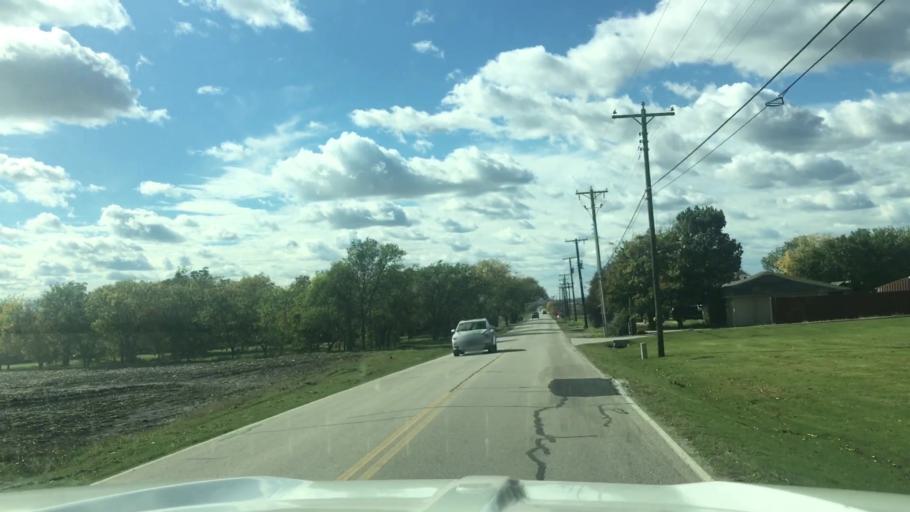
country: US
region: Texas
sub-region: Collin County
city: Prosper
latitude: 33.2337
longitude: -96.8038
